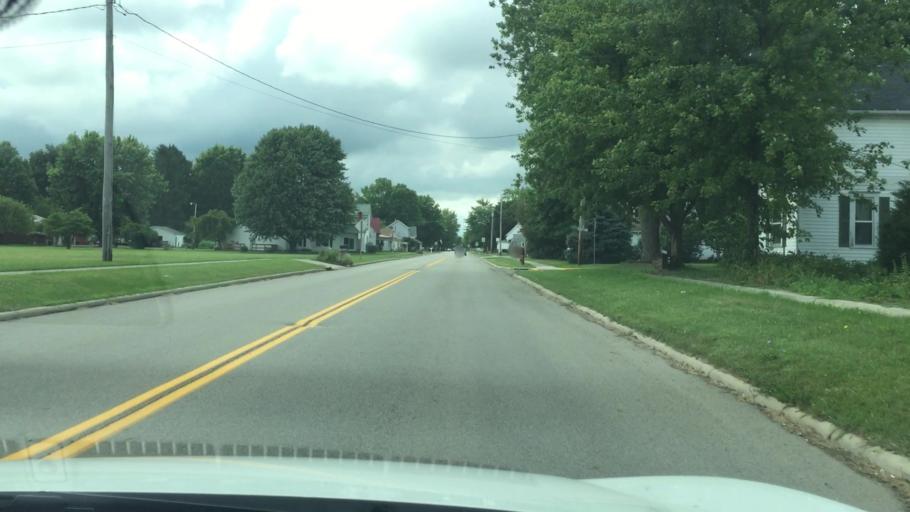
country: US
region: Ohio
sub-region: Champaign County
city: North Lewisburg
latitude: 40.2227
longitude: -83.5491
